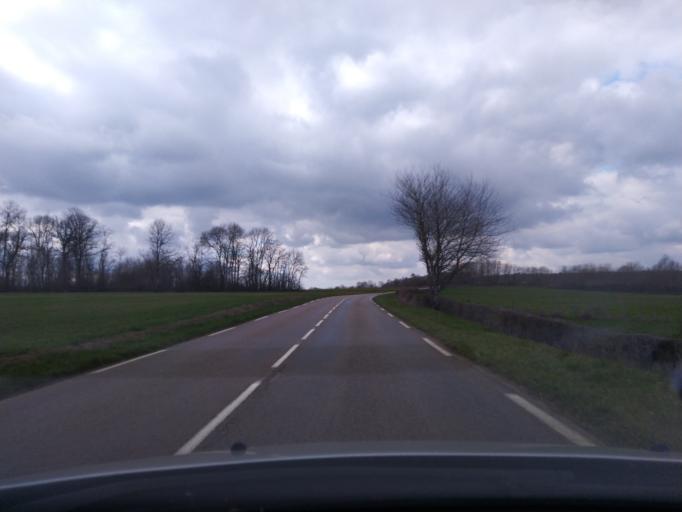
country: FR
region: Bourgogne
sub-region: Departement de l'Yonne
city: Avallon
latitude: 47.5199
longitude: 3.9664
